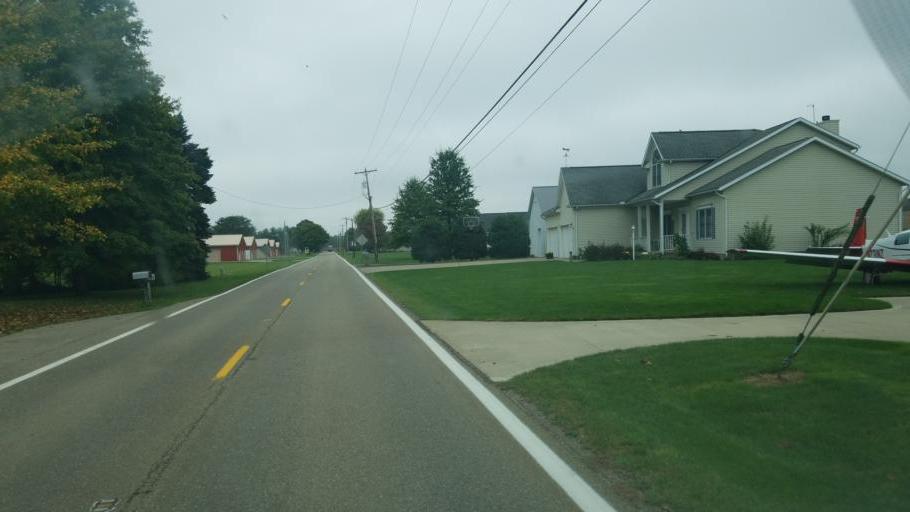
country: US
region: Ohio
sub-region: Stark County
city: Beach City
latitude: 40.6457
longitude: -81.5506
